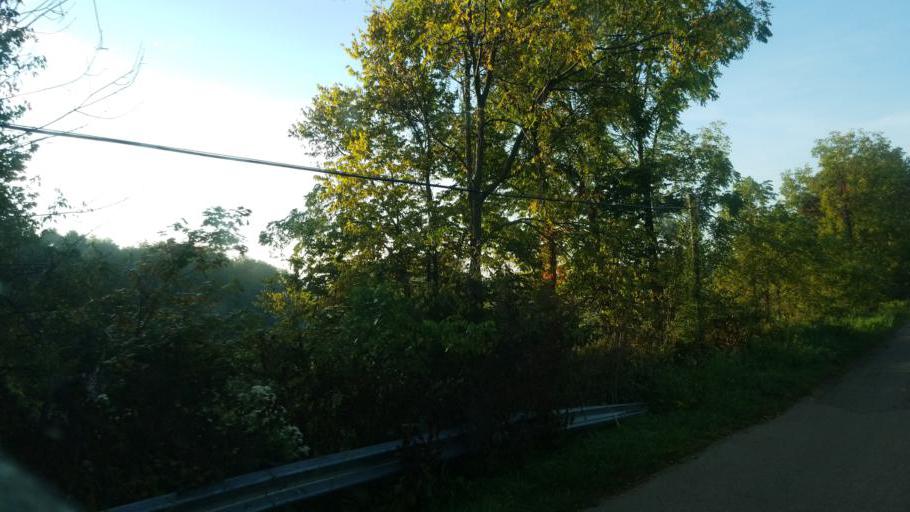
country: US
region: Ohio
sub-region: Knox County
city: Mount Vernon
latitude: 40.4044
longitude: -82.5636
